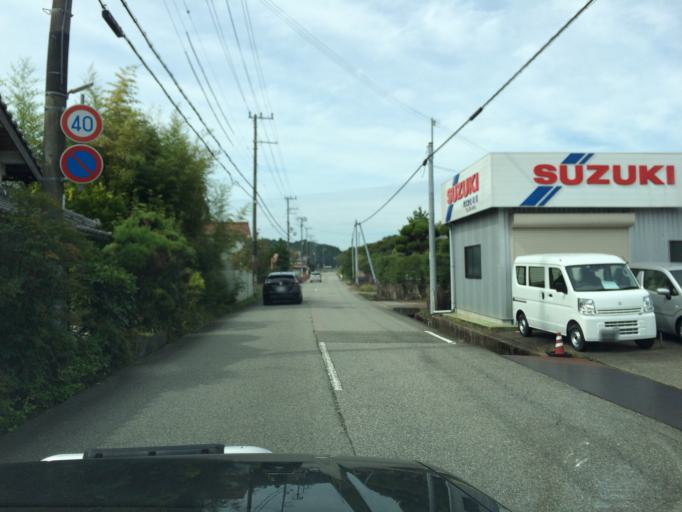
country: JP
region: Hyogo
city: Sasayama
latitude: 35.0687
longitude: 135.2753
